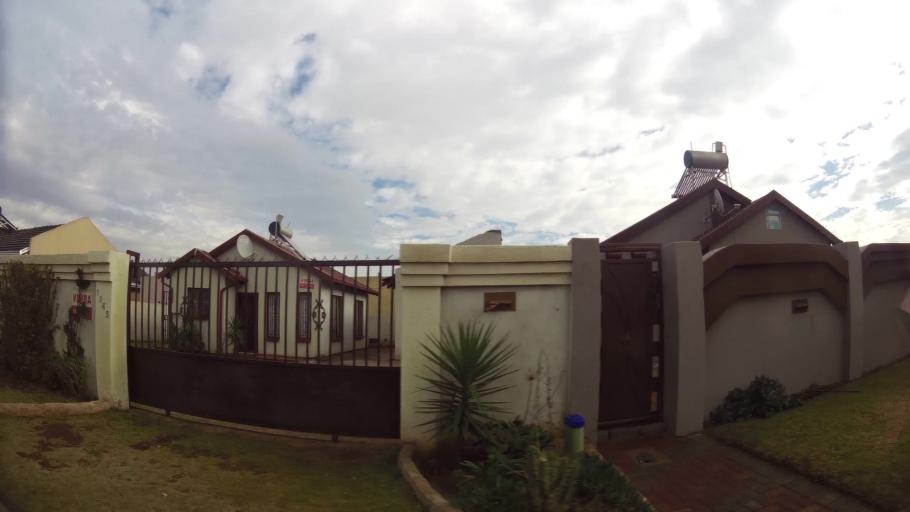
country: ZA
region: Gauteng
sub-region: Ekurhuleni Metropolitan Municipality
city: Germiston
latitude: -26.3329
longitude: 28.1961
